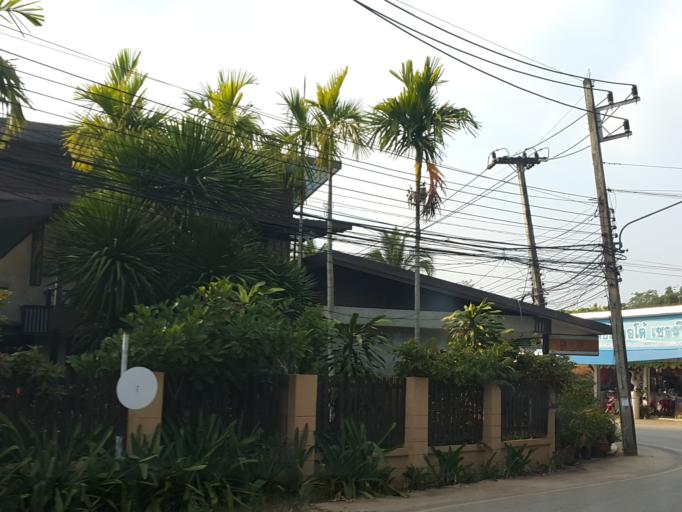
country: TH
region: Chiang Mai
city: Mae On
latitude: 18.9089
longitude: 99.2397
